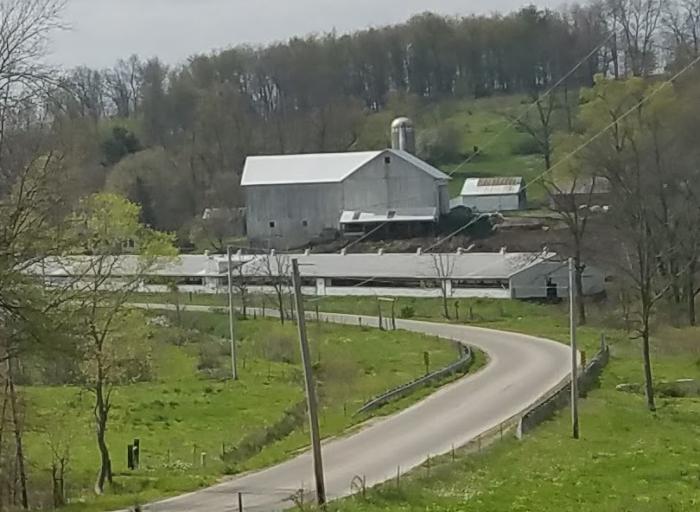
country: US
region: Ohio
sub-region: Sandusky County
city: Bellville
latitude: 40.5579
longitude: -82.3888
